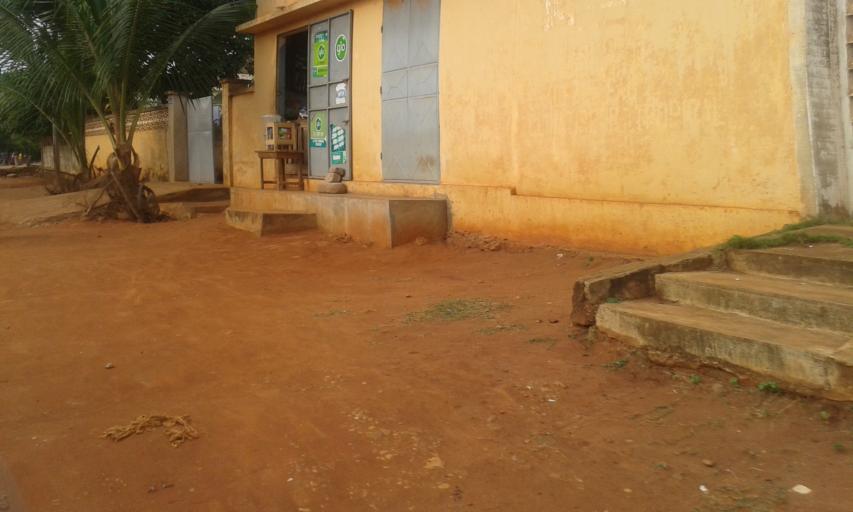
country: BJ
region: Queme
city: Porto-Novo
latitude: 6.4757
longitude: 2.6092
